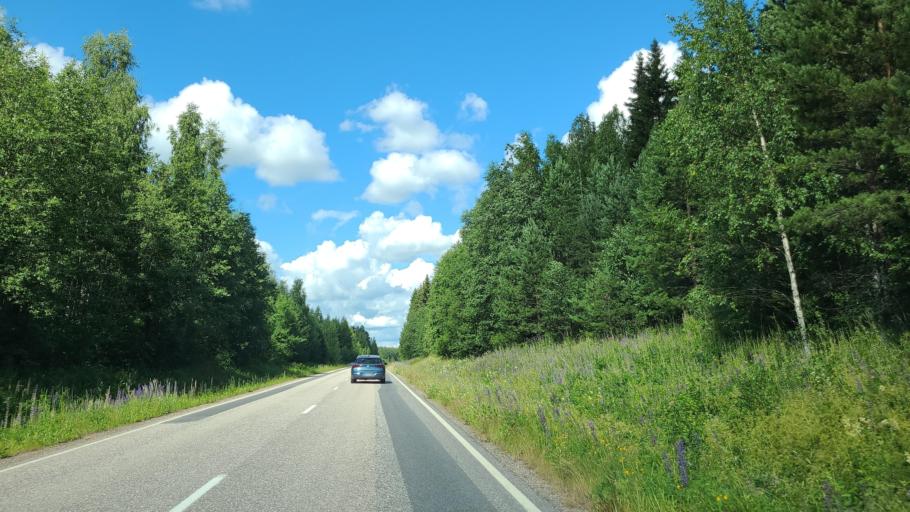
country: FI
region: Northern Savo
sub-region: Koillis-Savo
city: Kaavi
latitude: 62.9070
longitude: 28.7197
